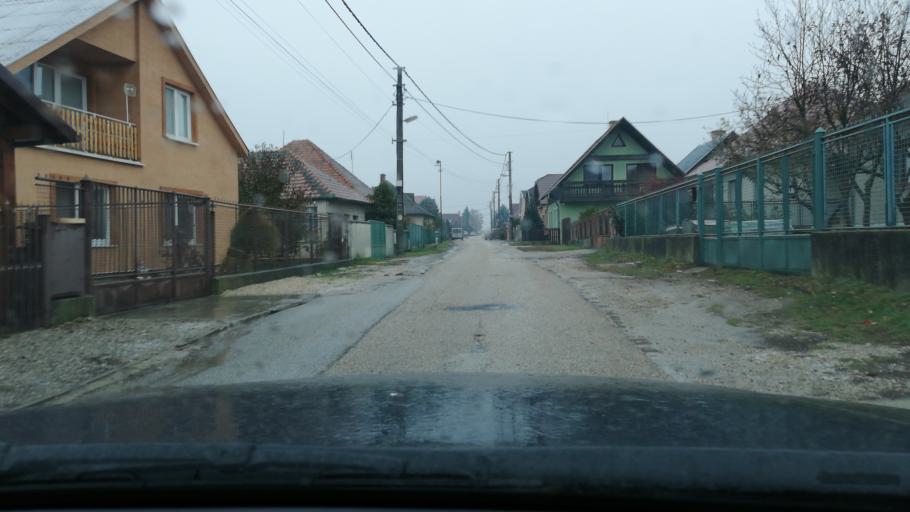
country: SK
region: Nitriansky
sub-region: Okres Nitra
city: Nitra
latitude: 48.3132
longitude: 17.9857
